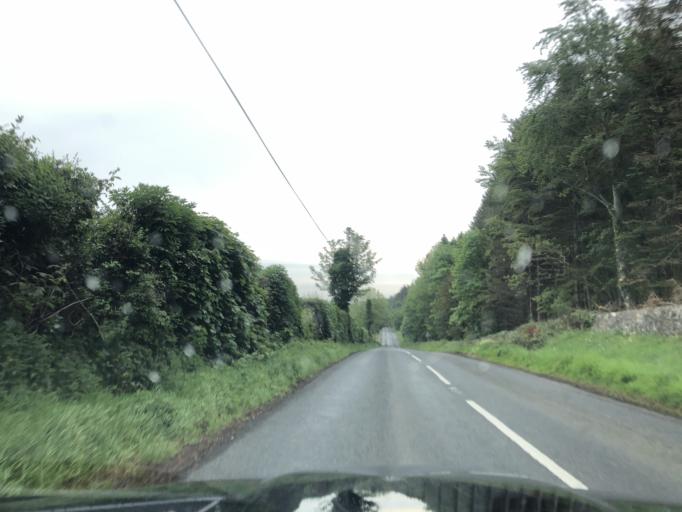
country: GB
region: Northern Ireland
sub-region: Down District
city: Castlewellan
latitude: 54.2249
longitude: -5.9512
